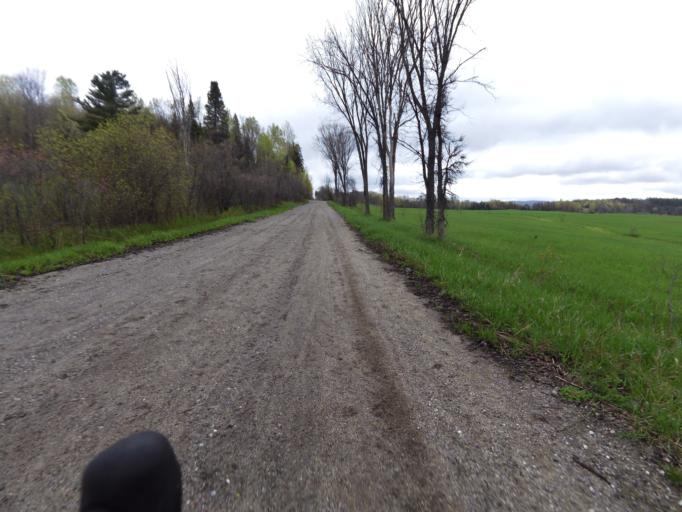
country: CA
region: Quebec
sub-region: Outaouais
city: Wakefield
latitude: 45.5876
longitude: -75.9031
